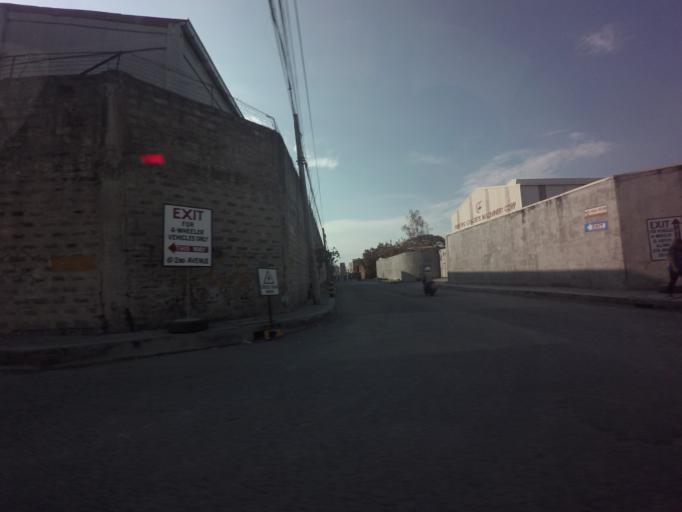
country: PH
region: Calabarzon
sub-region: Province of Rizal
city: Taguig
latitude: 14.4803
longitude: 121.0544
